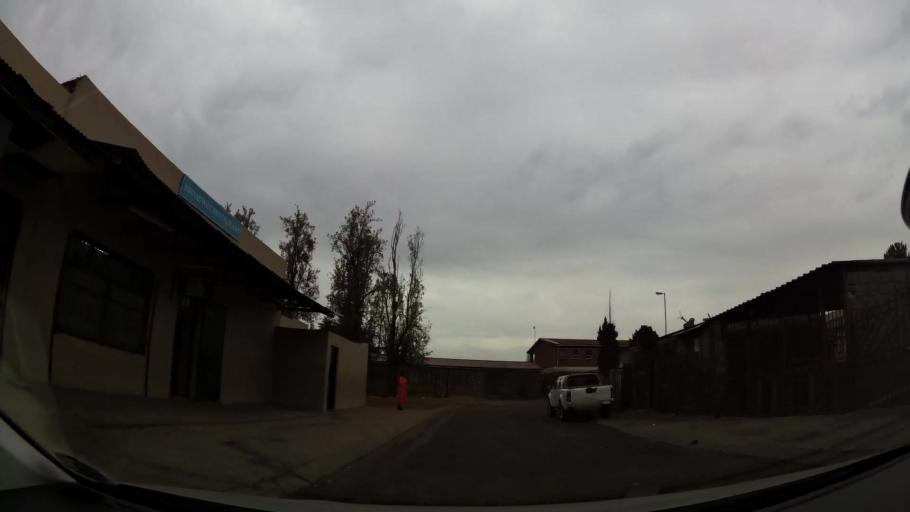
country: ZA
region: Gauteng
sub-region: City of Johannesburg Metropolitan Municipality
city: Soweto
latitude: -26.2519
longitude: 27.8725
